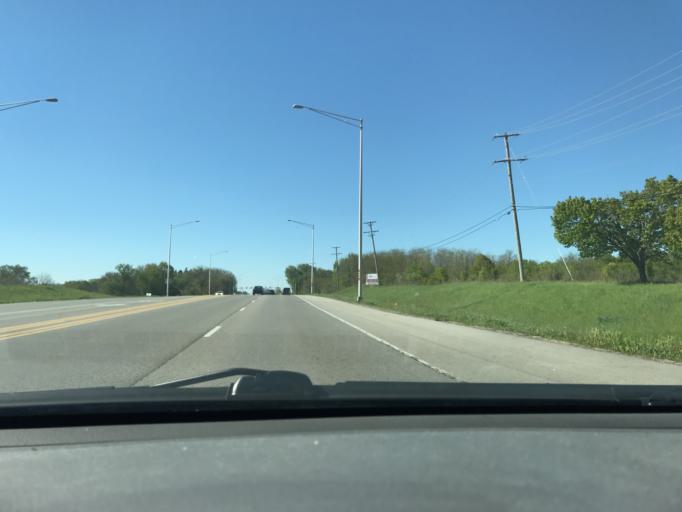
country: US
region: Illinois
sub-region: Kane County
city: Sleepy Hollow
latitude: 42.1077
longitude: -88.3351
